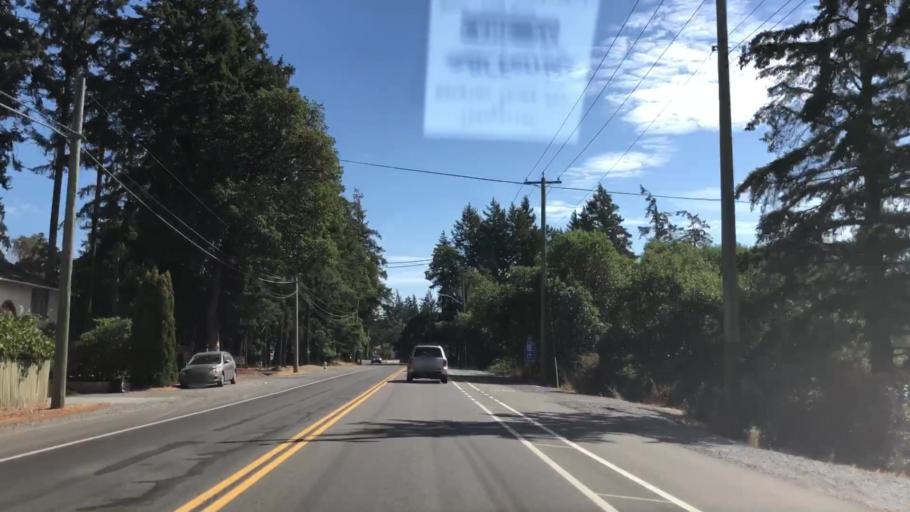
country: CA
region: British Columbia
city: Colwood
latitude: 48.4299
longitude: -123.4944
